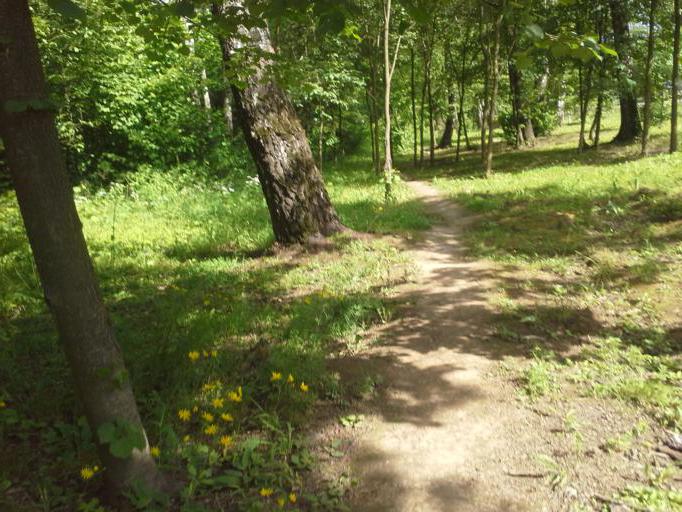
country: RU
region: Moskovskaya
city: Moskovskiy
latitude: 55.5813
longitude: 37.3632
